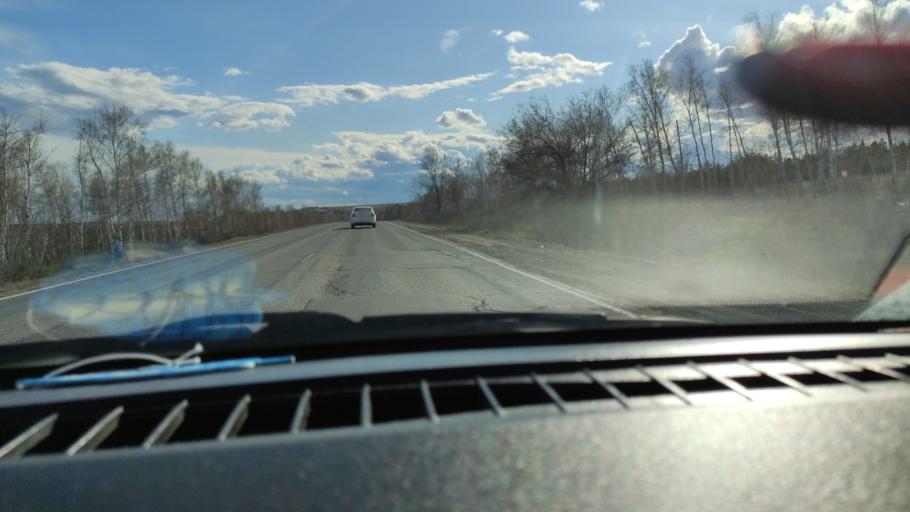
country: RU
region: Saratov
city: Sennoy
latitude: 52.1088
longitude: 46.8264
